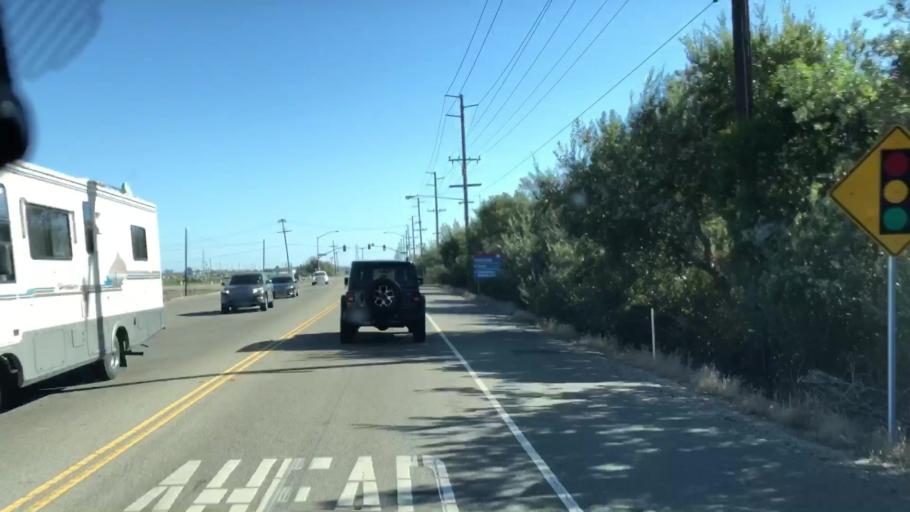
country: US
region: California
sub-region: Ventura County
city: Oxnard Shores
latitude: 34.2200
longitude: -119.2546
